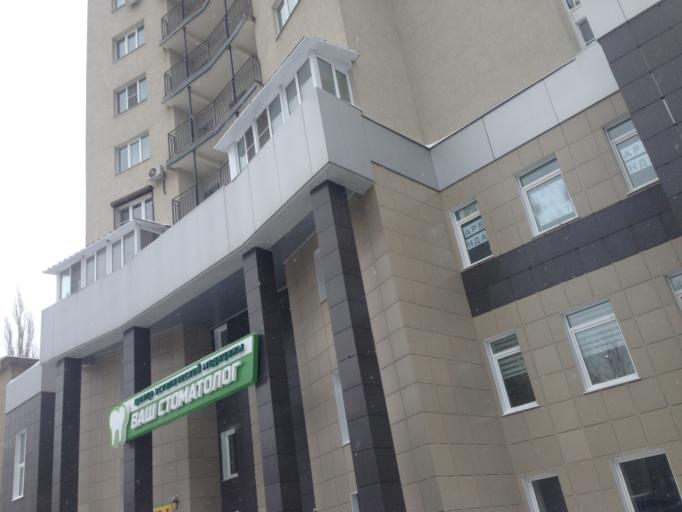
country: RU
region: Voronezj
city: Voronezh
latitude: 51.6558
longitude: 39.1524
